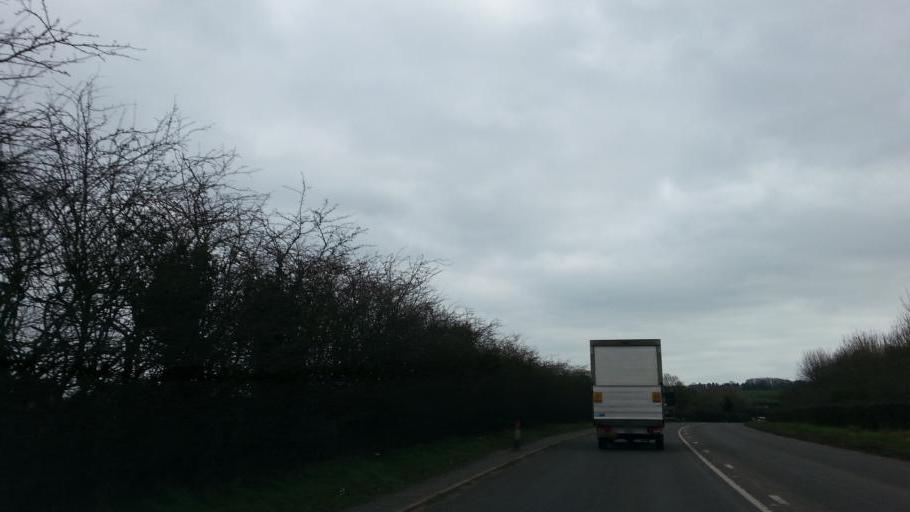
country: GB
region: England
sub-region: Staffordshire
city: Stone
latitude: 52.8878
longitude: -2.1290
